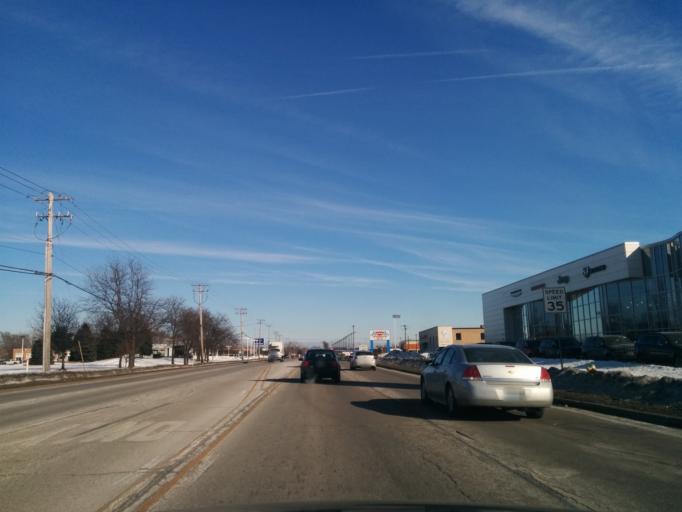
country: US
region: Illinois
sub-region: DuPage County
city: Bensenville
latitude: 41.9311
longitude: -87.9455
